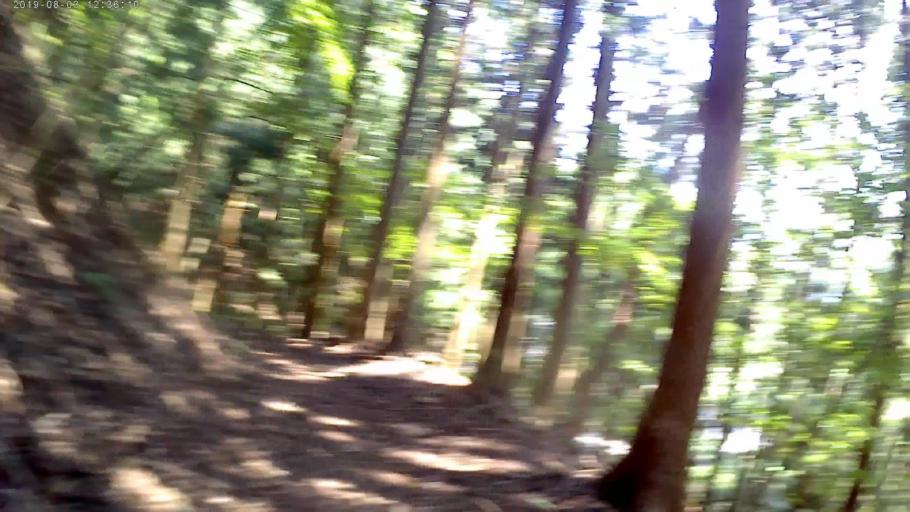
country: JP
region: Yamanashi
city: Enzan
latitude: 35.6071
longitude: 138.7928
